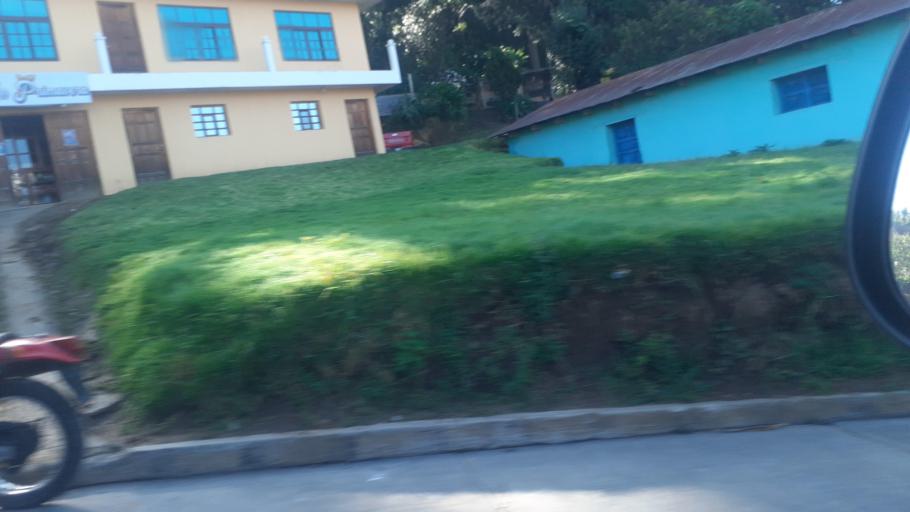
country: GT
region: Quetzaltenango
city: Cantel
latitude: 14.8168
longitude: -91.4497
